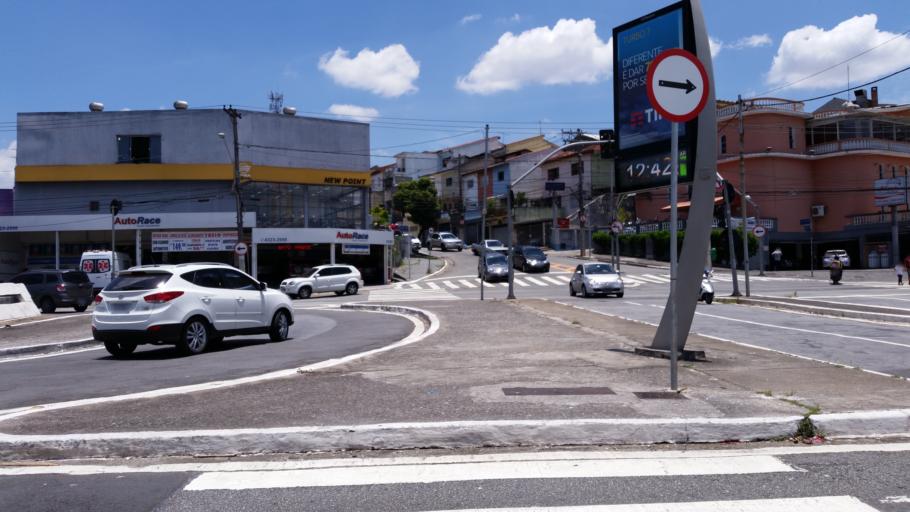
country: BR
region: Sao Paulo
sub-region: Sao Paulo
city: Sao Paulo
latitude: -23.5855
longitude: -46.6183
